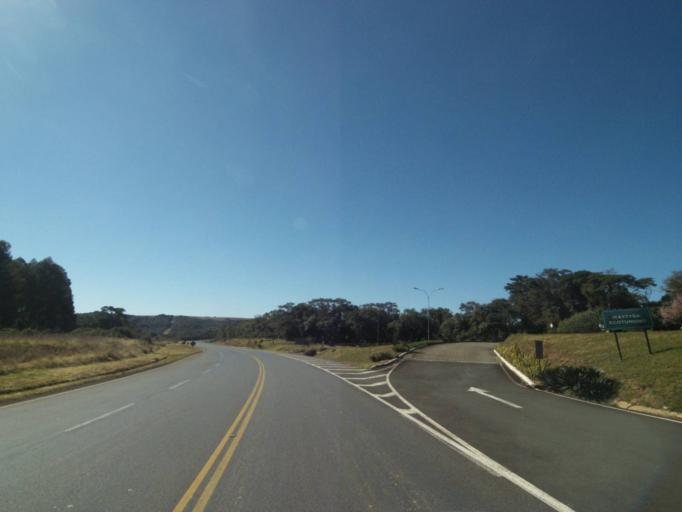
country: BR
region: Parana
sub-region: Tibagi
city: Tibagi
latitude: -24.4062
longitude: -50.3439
